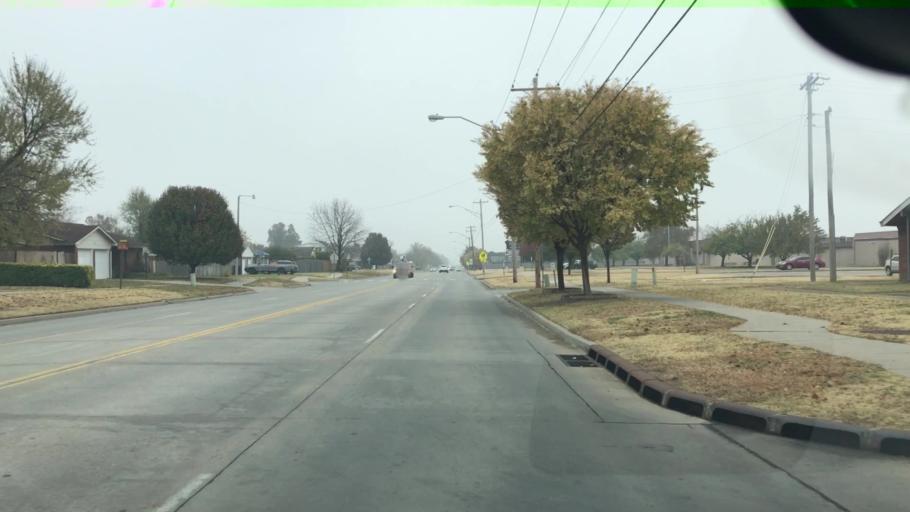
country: US
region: Oklahoma
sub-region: Cleveland County
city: Moore
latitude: 35.3469
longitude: -97.5122
